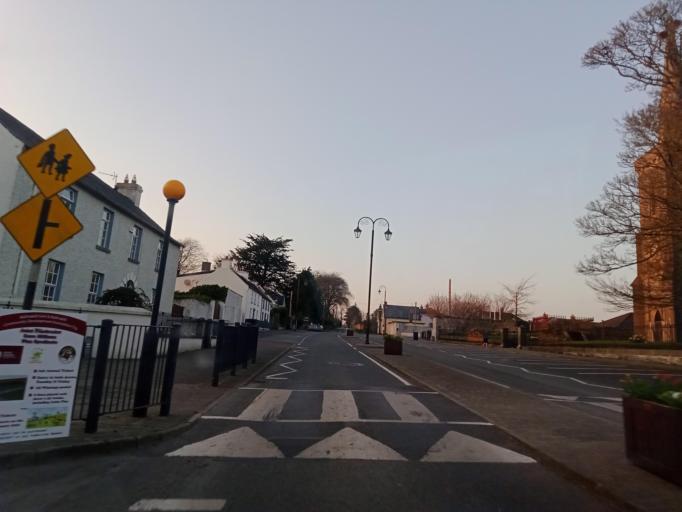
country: IE
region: Leinster
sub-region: Laois
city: Abbeyleix
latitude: 52.8753
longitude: -7.3087
